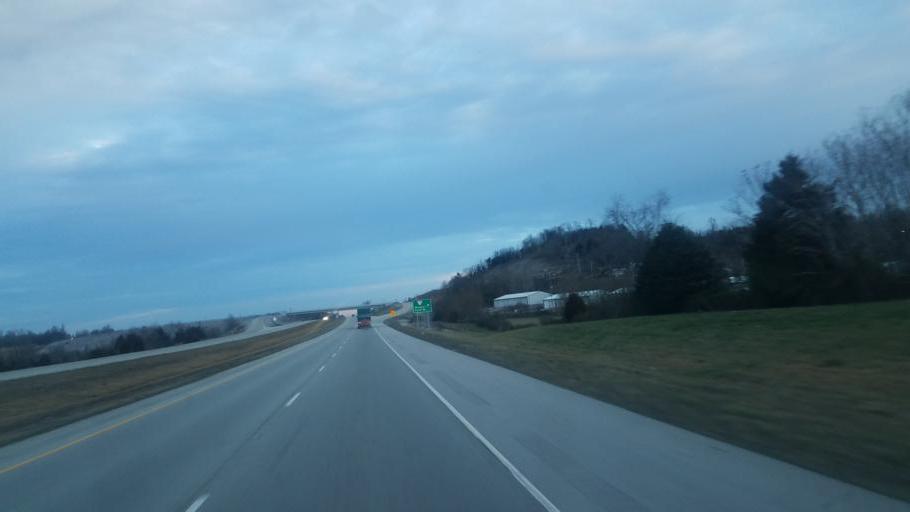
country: US
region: Tennessee
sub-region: White County
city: Sparta
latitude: 35.9864
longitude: -85.4997
